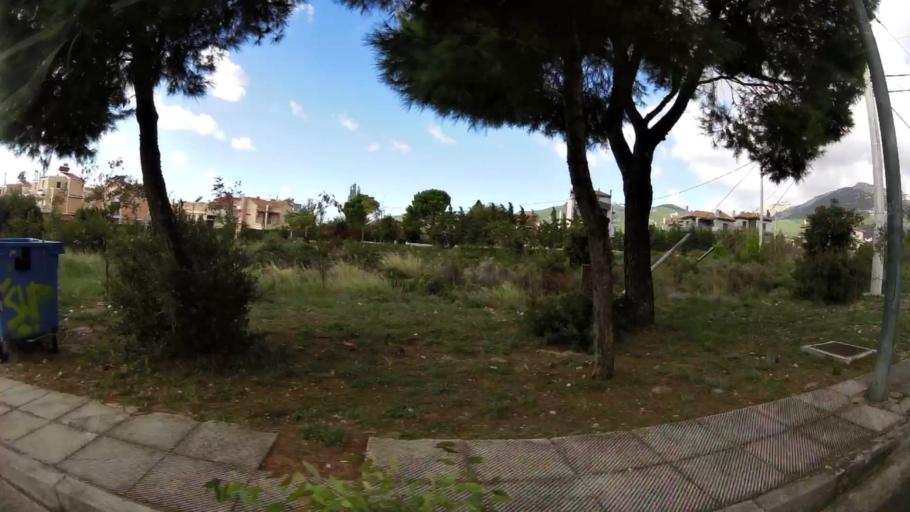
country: GR
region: Attica
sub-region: Nomarchia Anatolikis Attikis
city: Thrakomakedones
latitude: 38.1214
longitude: 23.7530
